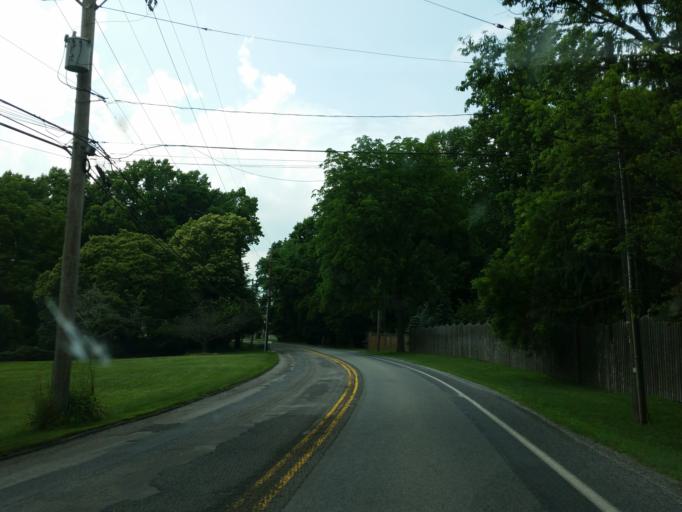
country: US
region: Pennsylvania
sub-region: Chester County
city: West Grove
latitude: 39.7767
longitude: -75.8639
